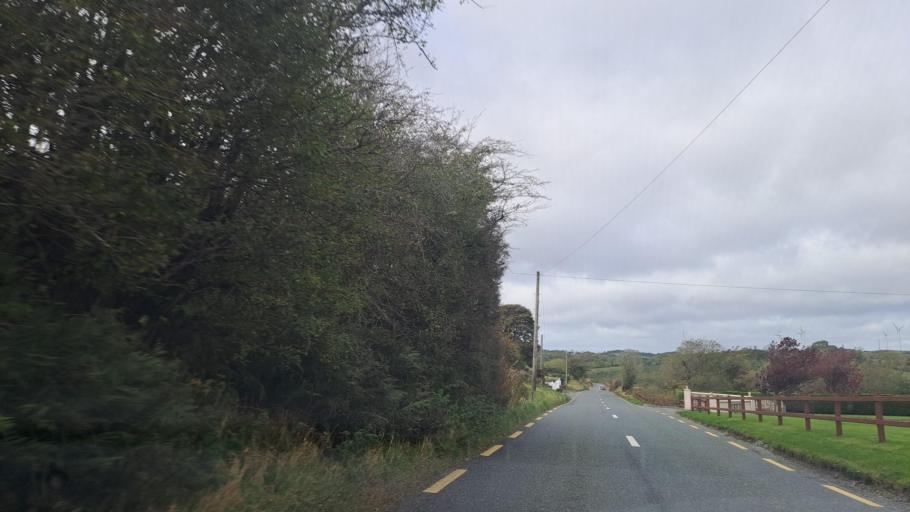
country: IE
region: Ulster
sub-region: An Cabhan
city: Bailieborough
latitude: 53.9321
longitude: -6.9031
